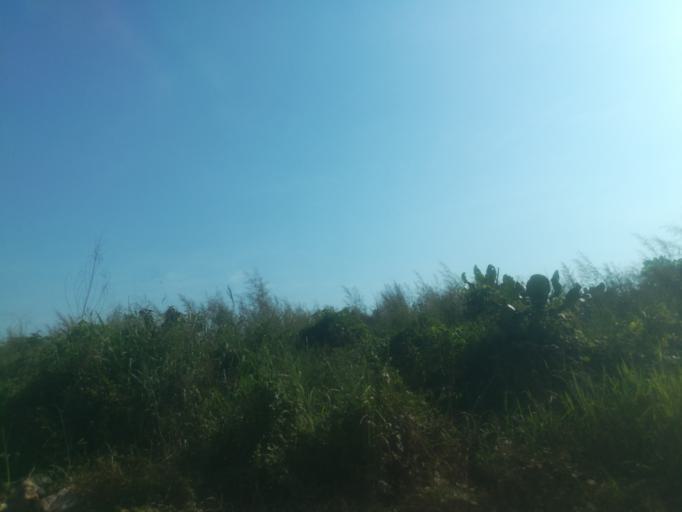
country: NG
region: Ogun
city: Abeokuta
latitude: 7.1405
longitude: 3.2605
